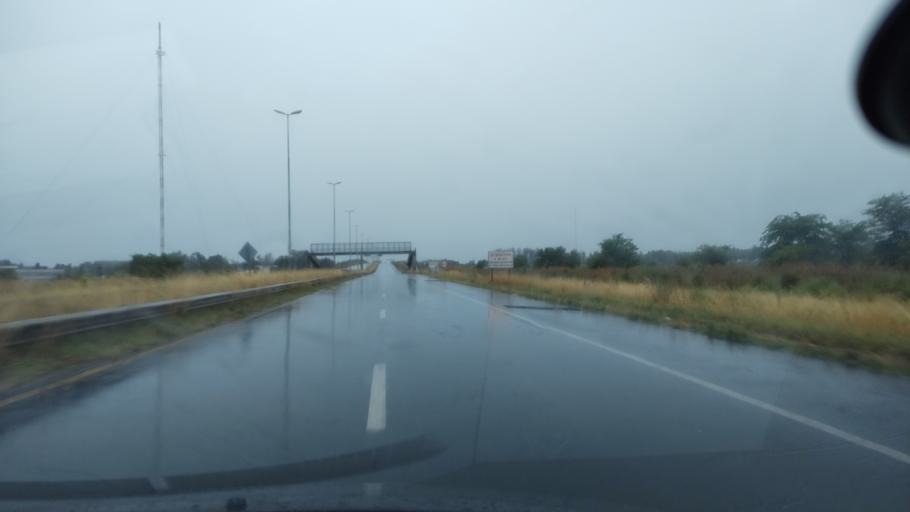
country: AR
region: Buenos Aires
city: Canuelas
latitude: -35.0242
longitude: -58.7373
